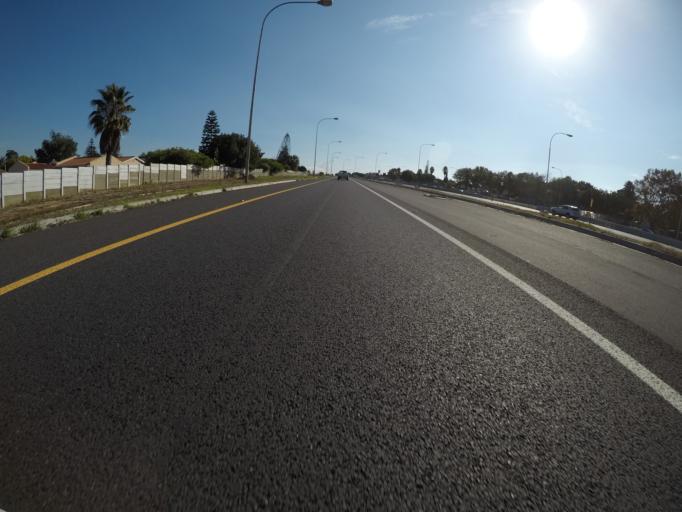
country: ZA
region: Western Cape
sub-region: City of Cape Town
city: Kraaifontein
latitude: -33.8743
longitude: 18.6661
